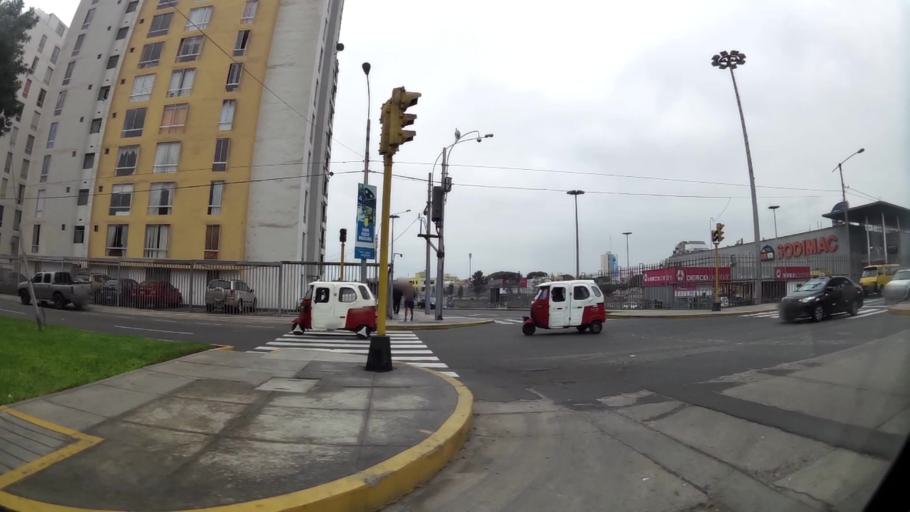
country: PE
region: Callao
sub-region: Callao
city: Callao
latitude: -12.0816
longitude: -77.0887
